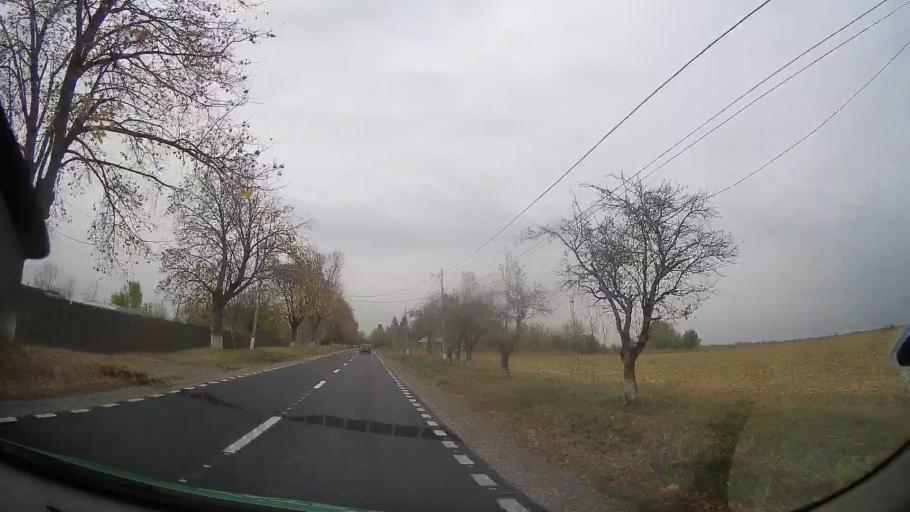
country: RO
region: Ilfov
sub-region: Comuna Nuci
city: Nuci
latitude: 44.7185
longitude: 26.3085
